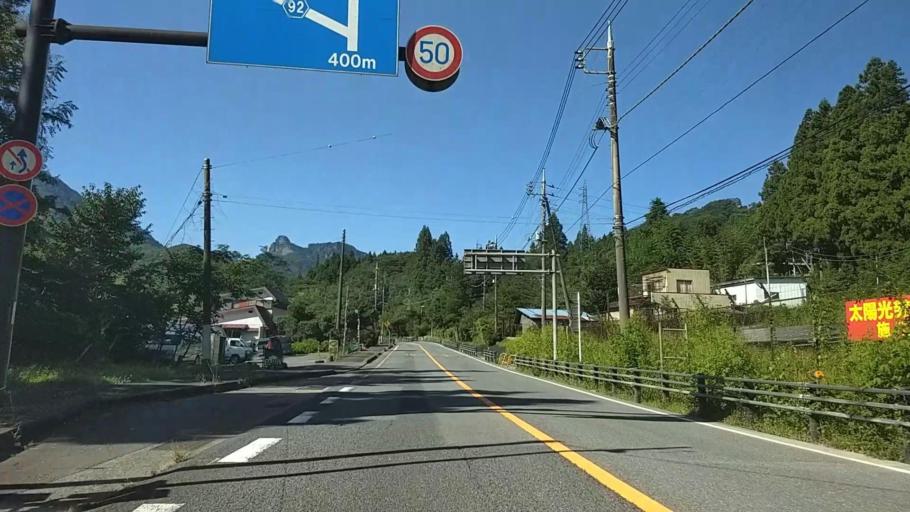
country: JP
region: Gunma
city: Annaka
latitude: 36.3283
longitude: 138.7083
